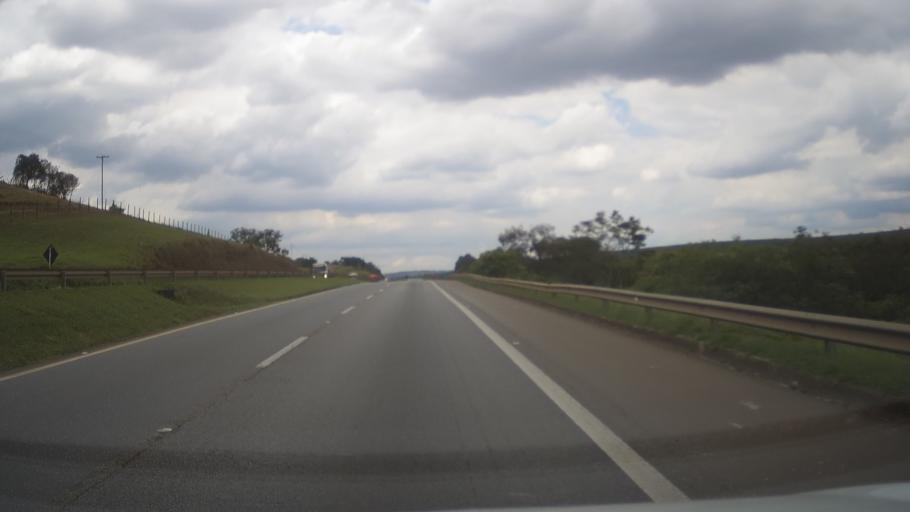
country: BR
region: Minas Gerais
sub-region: Tres Coracoes
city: Tres Coracoes
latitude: -21.5169
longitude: -45.2216
